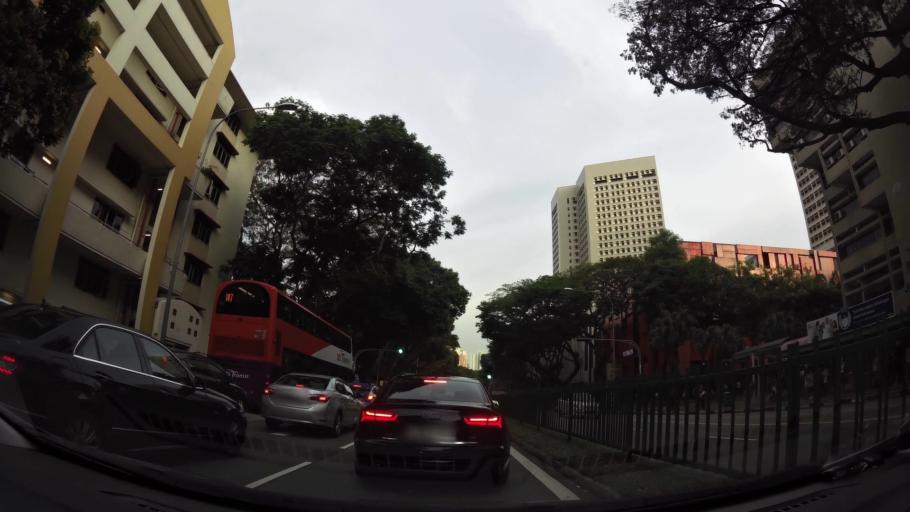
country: SG
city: Singapore
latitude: 1.2842
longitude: 103.8178
